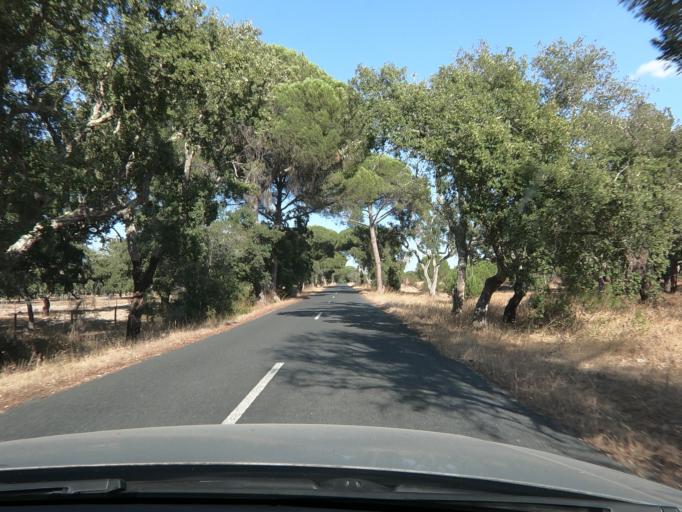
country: PT
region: Setubal
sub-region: Alcacer do Sal
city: Alcacer do Sal
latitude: 38.2652
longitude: -8.3270
